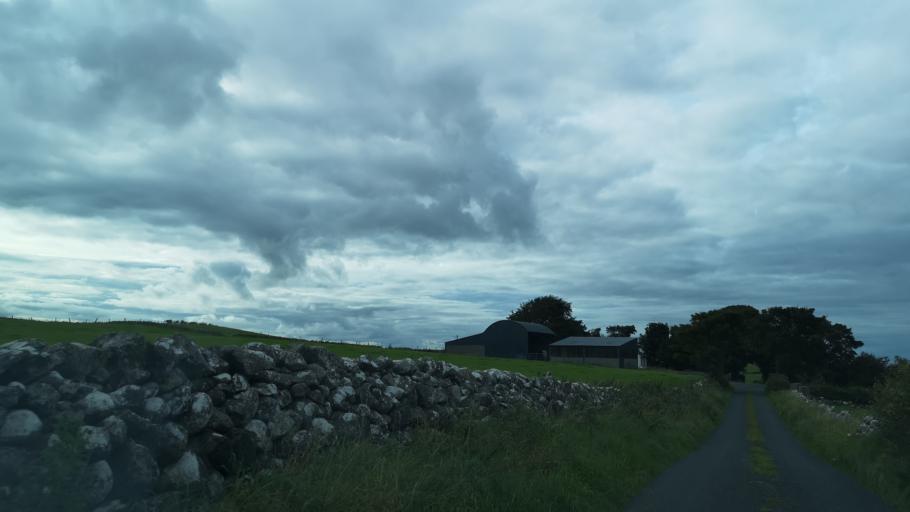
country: IE
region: Connaught
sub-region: County Galway
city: Ballinasloe
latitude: 53.3725
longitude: -8.1657
